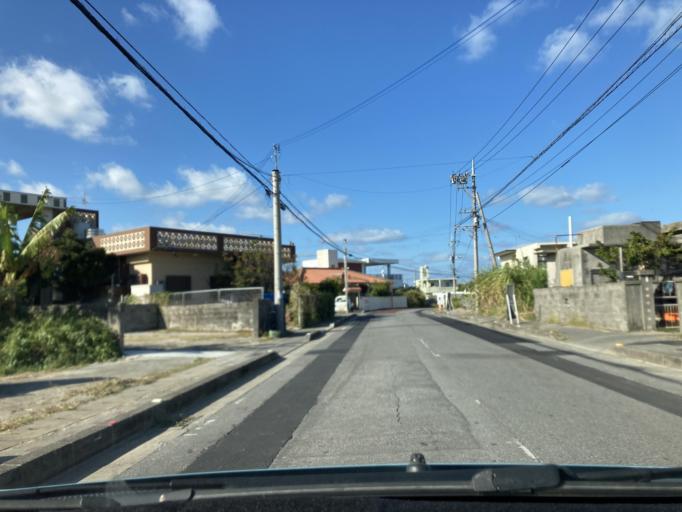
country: JP
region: Okinawa
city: Katsuren-haebaru
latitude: 26.3162
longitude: 127.9090
